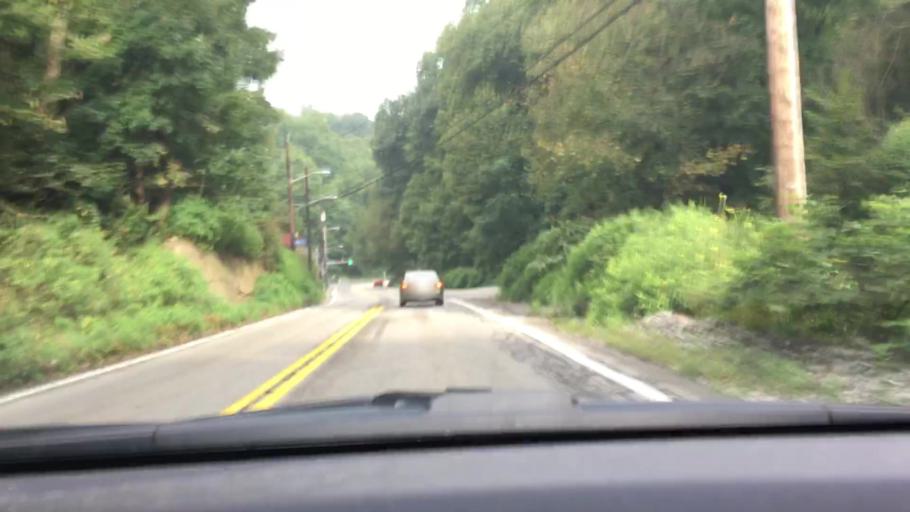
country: US
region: Pennsylvania
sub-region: Allegheny County
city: West Homestead
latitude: 40.3789
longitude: -79.9233
